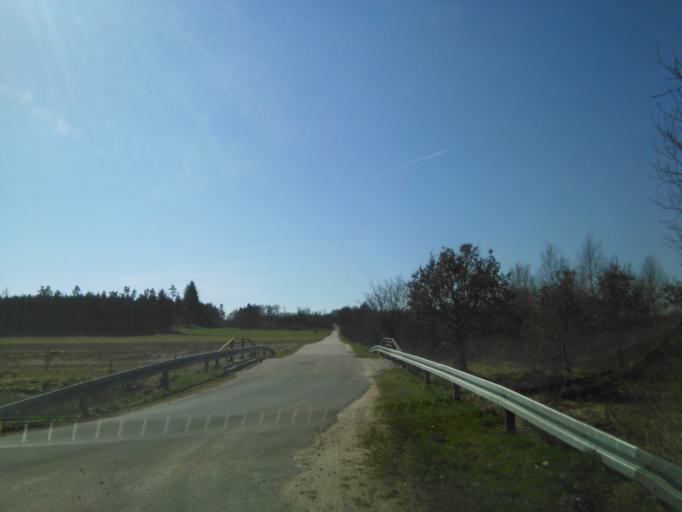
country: DK
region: Central Jutland
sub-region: Horsens Kommune
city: Braedstrup
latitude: 55.9750
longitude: 9.4977
